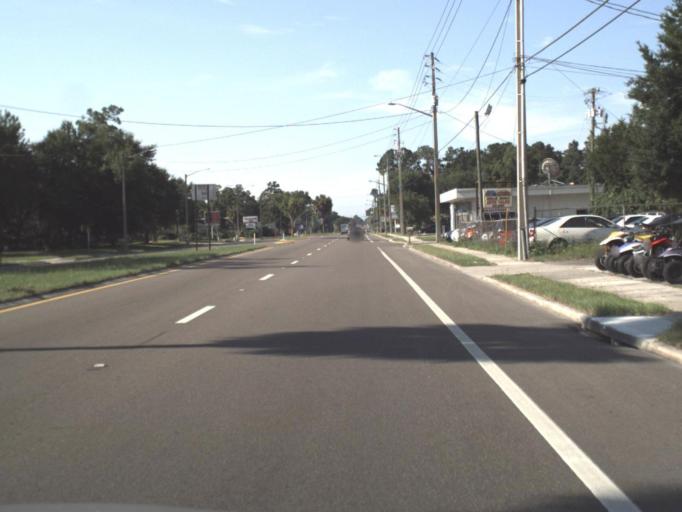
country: US
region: Florida
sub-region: Alachua County
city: Gainesville
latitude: 29.6939
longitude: -82.3391
